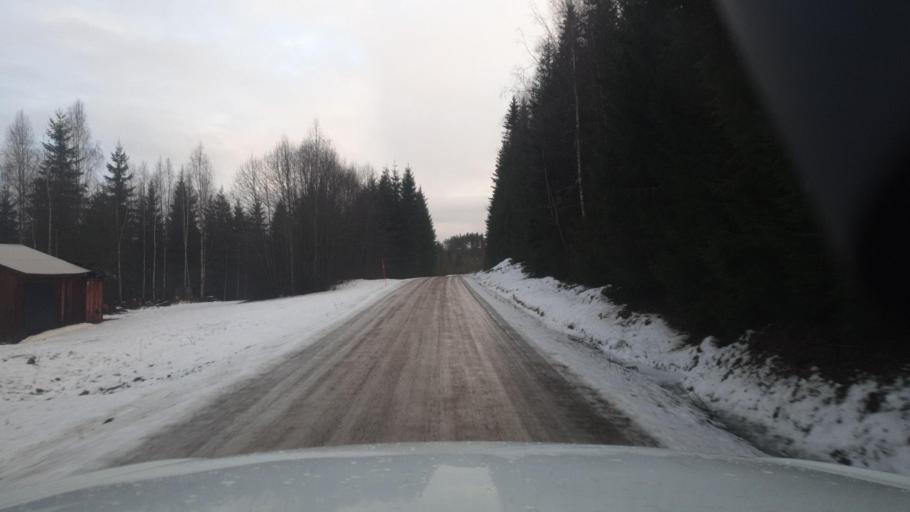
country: SE
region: Vaermland
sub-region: Torsby Kommun
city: Torsby
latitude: 59.9811
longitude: 12.8388
